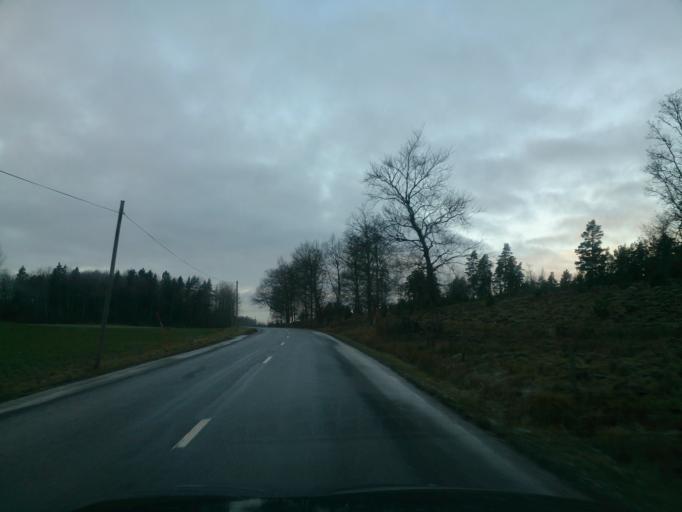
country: SE
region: OEstergoetland
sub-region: Norrkopings Kommun
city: Kimstad
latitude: 58.3903
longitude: 15.9816
